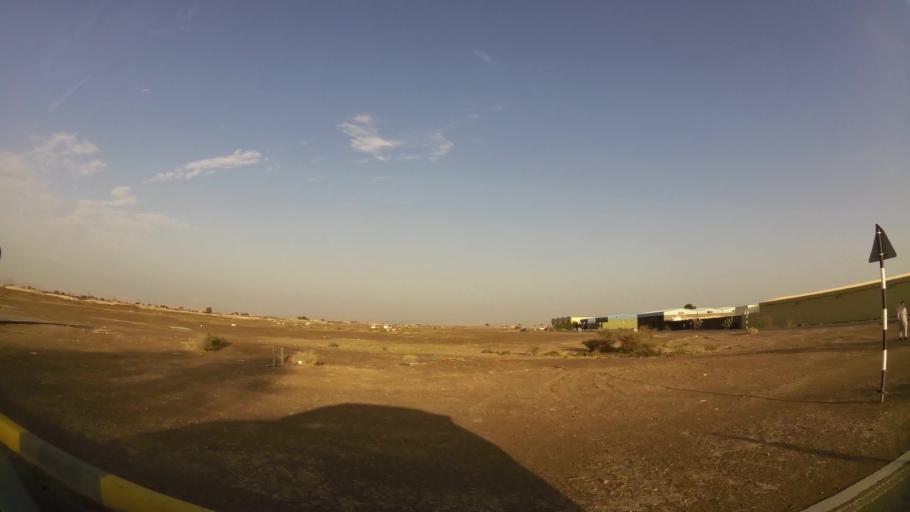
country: AE
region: Abu Dhabi
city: Al Ain
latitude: 24.1545
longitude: 55.8380
